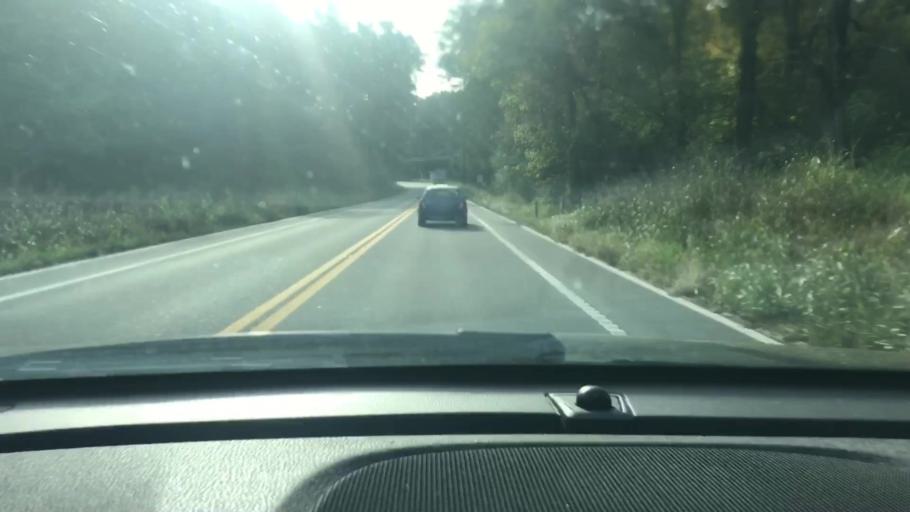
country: US
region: Tennessee
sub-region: Williamson County
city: Fairview
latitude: 36.0138
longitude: -87.0423
